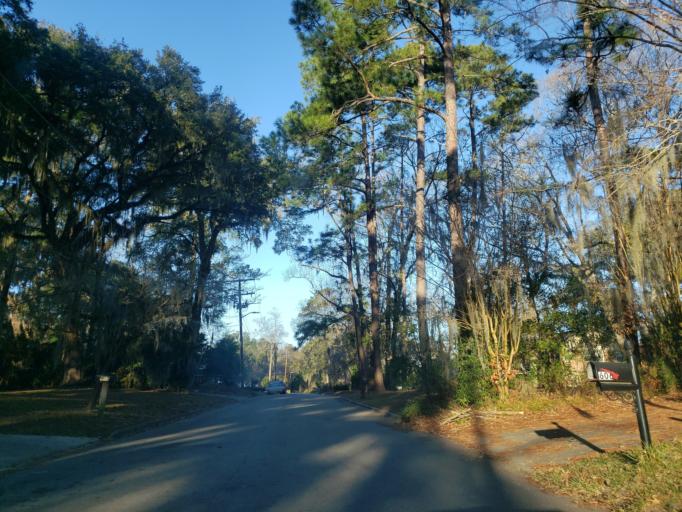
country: US
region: Georgia
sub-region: Chatham County
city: Isle of Hope
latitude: 32.0140
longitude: -81.1015
